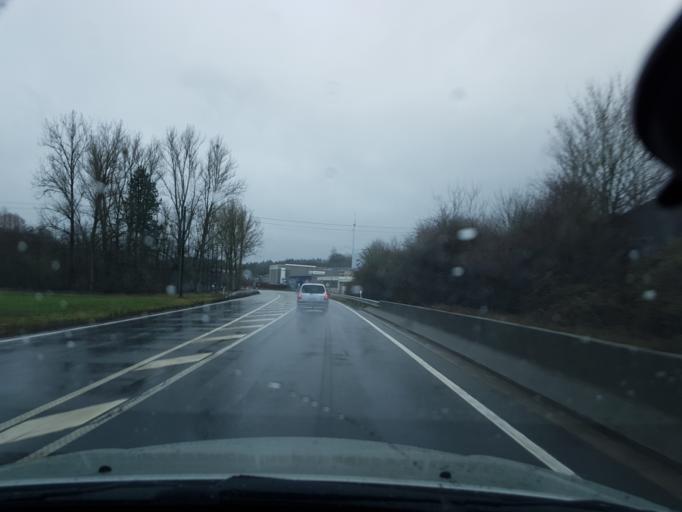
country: DE
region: Rheinland-Pfalz
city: Birkenfeld
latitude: 49.6395
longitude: 7.1601
